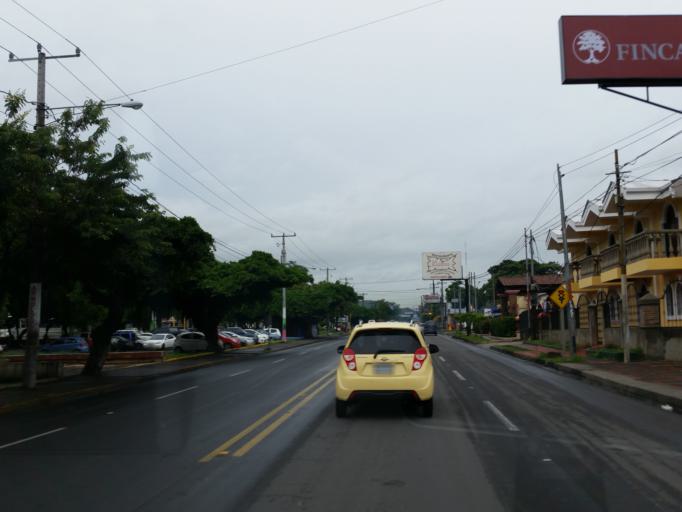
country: NI
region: Managua
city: Managua
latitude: 12.1451
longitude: -86.2906
